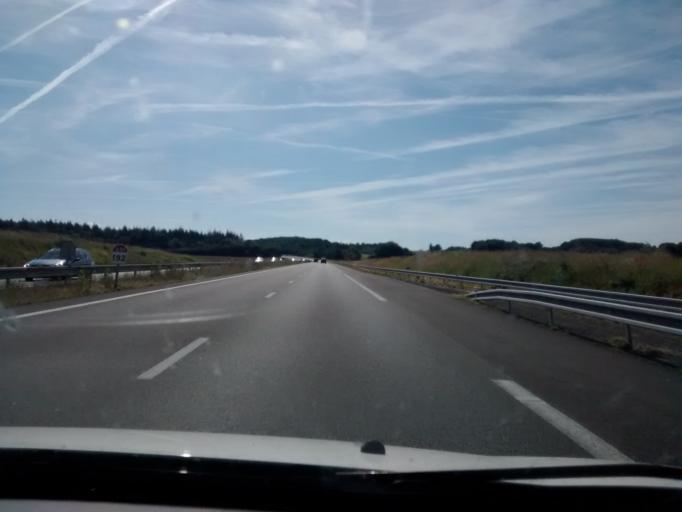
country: FR
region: Pays de la Loire
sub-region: Departement de la Sarthe
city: Louplande
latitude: 48.0138
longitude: -0.0802
